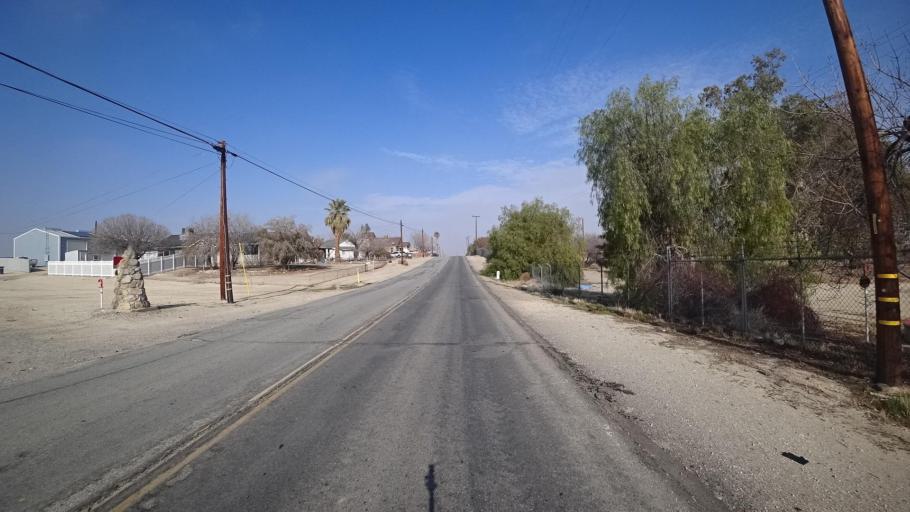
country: US
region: California
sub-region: Kern County
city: Ford City
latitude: 35.1675
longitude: -119.4653
